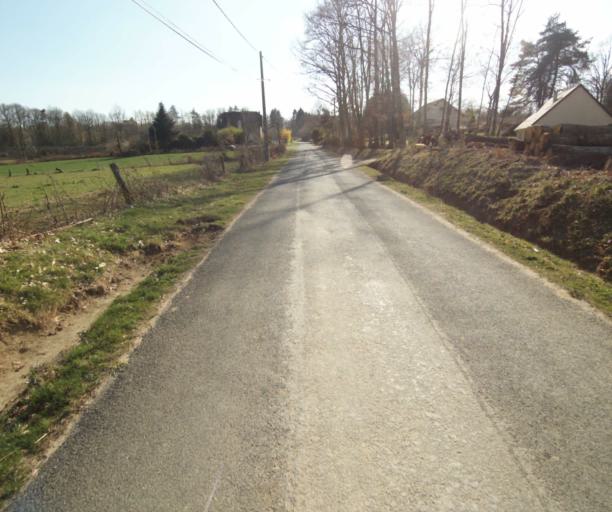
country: FR
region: Limousin
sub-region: Departement de la Correze
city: Saint-Mexant
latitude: 45.3191
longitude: 1.6225
